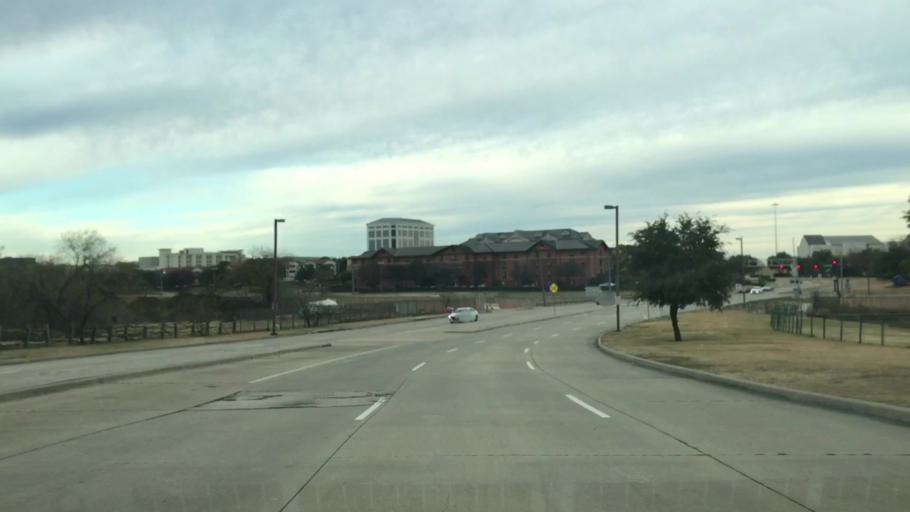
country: US
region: Texas
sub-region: Dallas County
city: Irving
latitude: 32.8807
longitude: -96.9532
